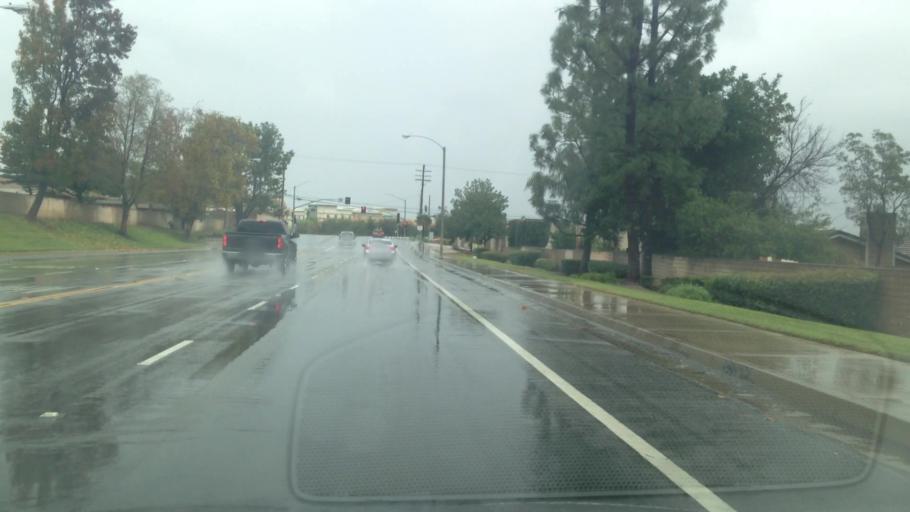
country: US
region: California
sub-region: Riverside County
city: Home Gardens
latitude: 33.9020
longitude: -117.4993
